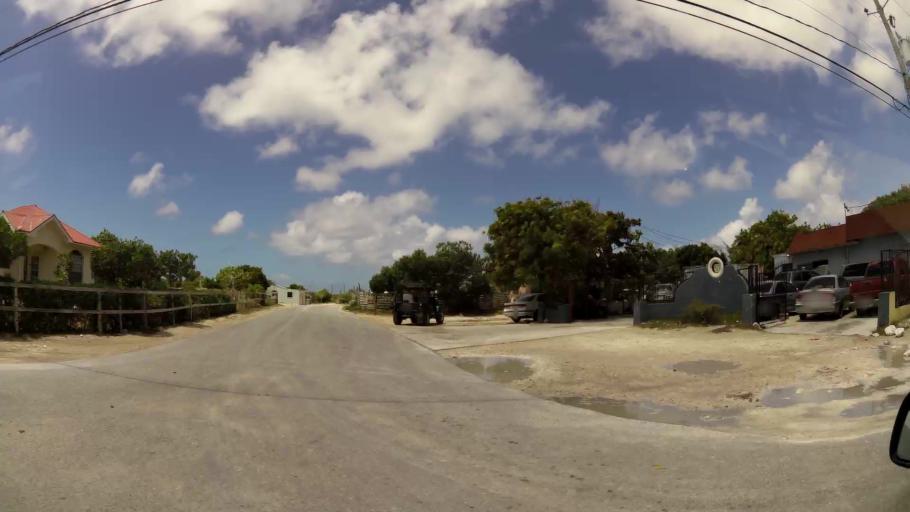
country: TC
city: Cockburn Town
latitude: 21.4577
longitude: -71.1419
